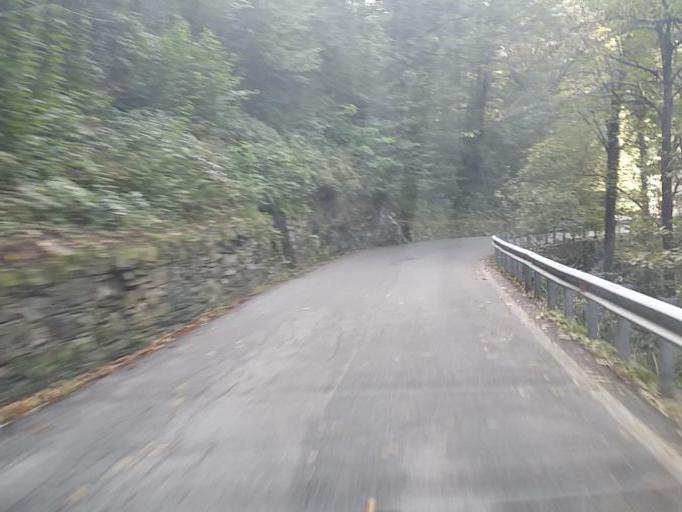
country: IT
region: Piedmont
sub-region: Provincia Verbano-Cusio-Ossola
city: Falmenta
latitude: 46.0746
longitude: 8.6026
